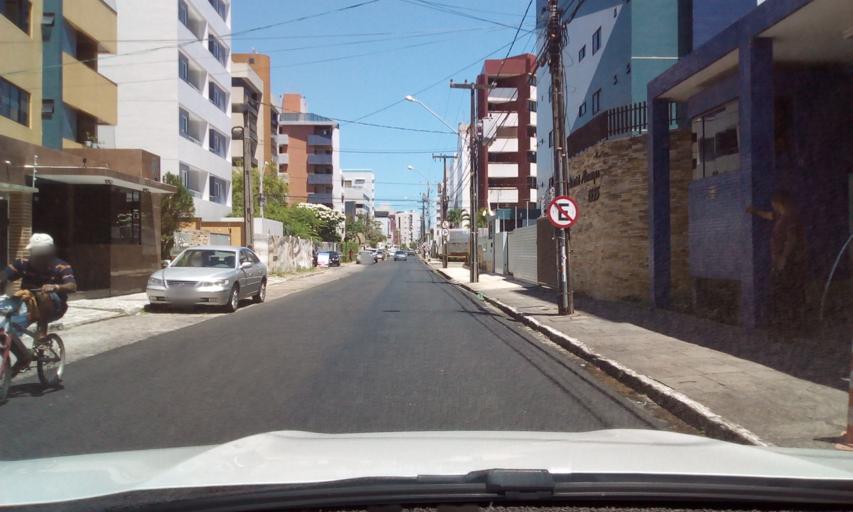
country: BR
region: Paraiba
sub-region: Joao Pessoa
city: Joao Pessoa
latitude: -7.1271
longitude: -34.8249
